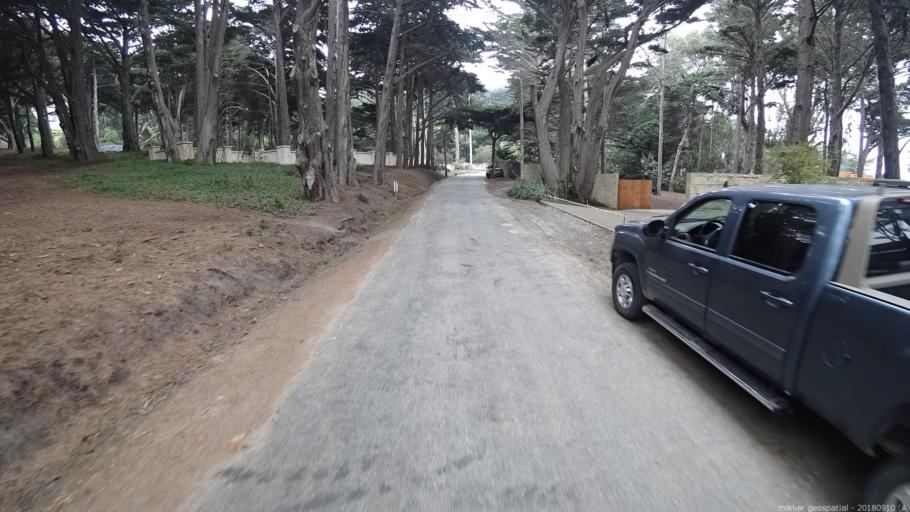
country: US
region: California
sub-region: Monterey County
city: Carmel-by-the-Sea
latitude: 36.4943
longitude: -121.9390
